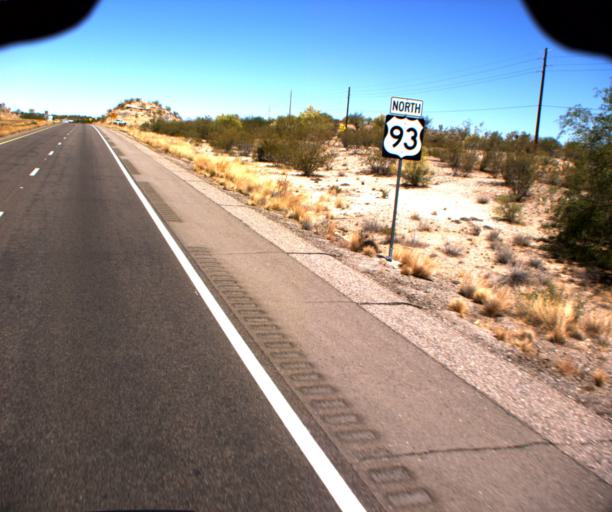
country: US
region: Arizona
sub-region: Maricopa County
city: Wickenburg
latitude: 34.0241
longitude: -112.8074
